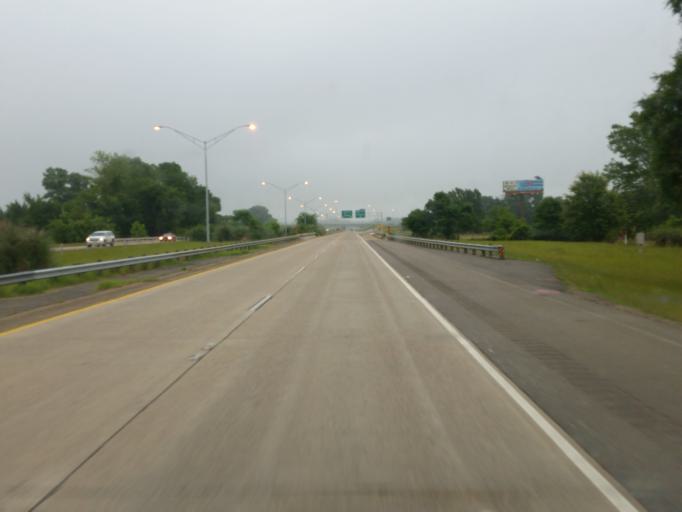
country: US
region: Louisiana
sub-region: Bossier Parish
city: Red Chute
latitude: 32.5367
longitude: -93.6413
